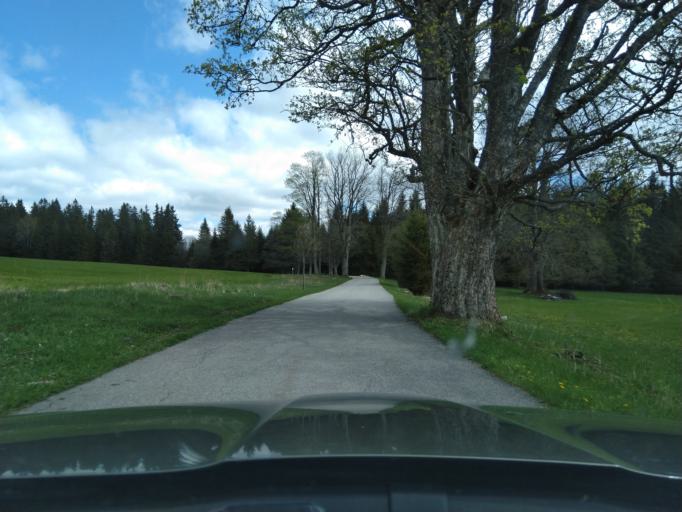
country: CZ
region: Jihocesky
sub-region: Okres Prachatice
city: Borova Lada
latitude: 49.0022
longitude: 13.6952
